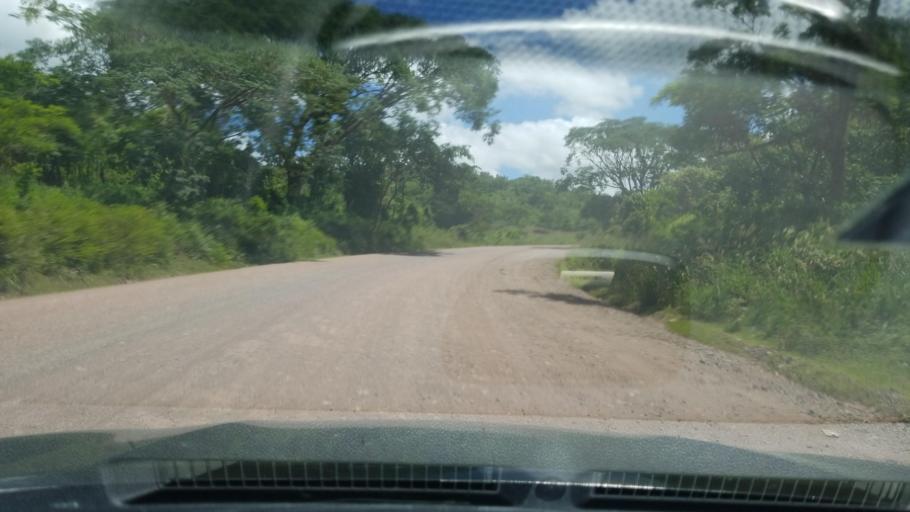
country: HN
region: Francisco Morazan
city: San Juan de Flores
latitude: 14.3224
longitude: -87.0468
